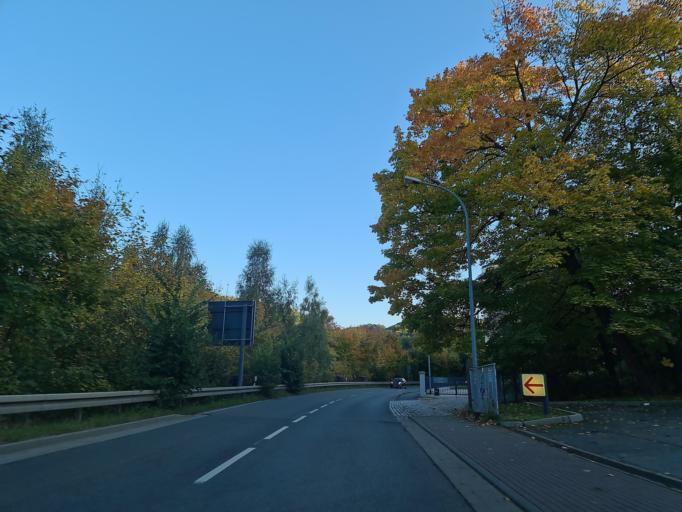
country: DE
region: Thuringia
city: Greiz
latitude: 50.6470
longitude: 12.1952
